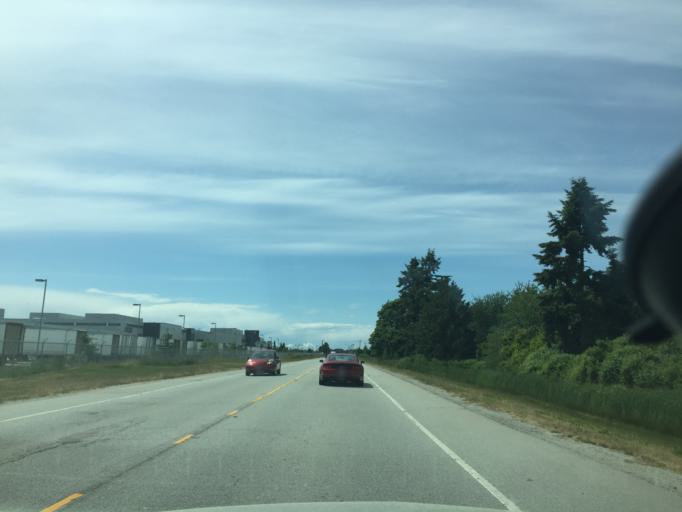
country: CA
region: British Columbia
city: Richmond
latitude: 49.2058
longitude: -123.1638
